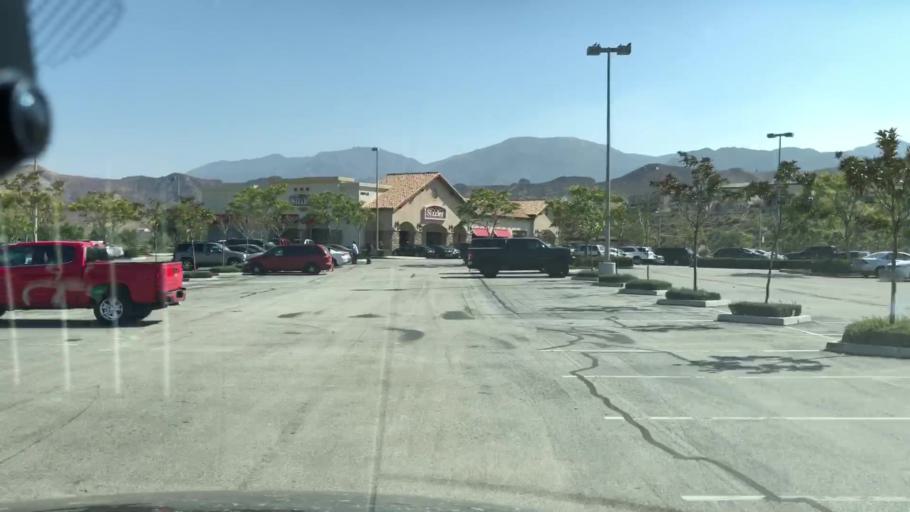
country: US
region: California
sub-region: Los Angeles County
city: Santa Clarita
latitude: 34.3954
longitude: -118.4609
